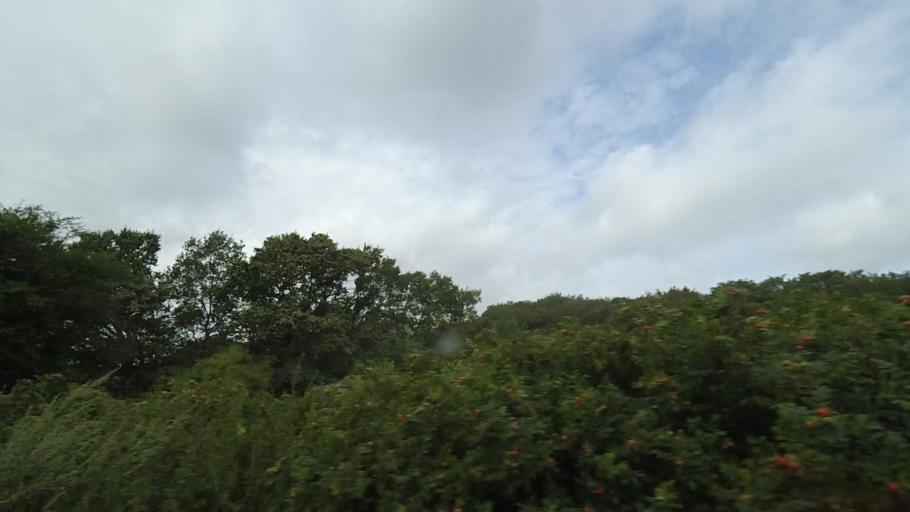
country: DK
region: Central Jutland
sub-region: Syddjurs Kommune
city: Ryomgard
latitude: 56.3965
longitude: 10.4888
